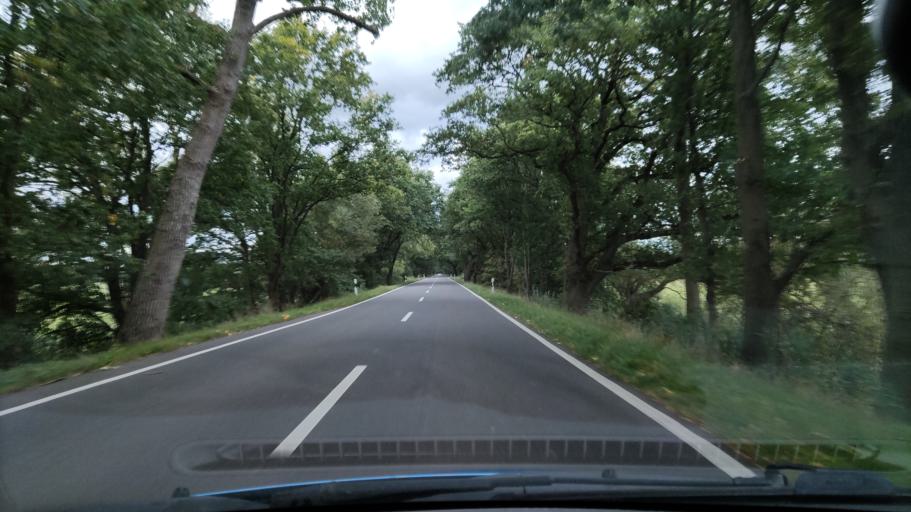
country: DE
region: Lower Saxony
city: Neu Darchau
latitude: 53.3363
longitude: 10.9479
